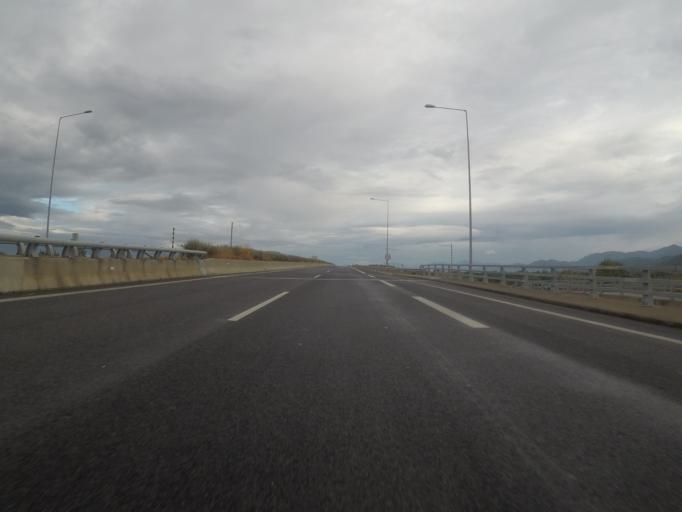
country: GR
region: Peloponnese
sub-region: Nomos Messinias
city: Thouria
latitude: 37.0771
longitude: 22.0432
